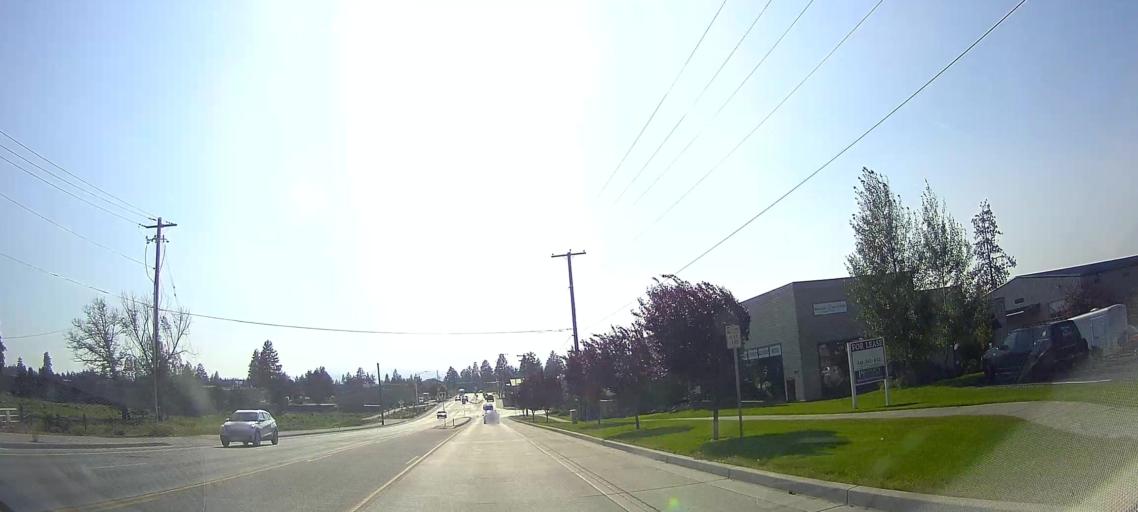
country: US
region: Oregon
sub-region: Deschutes County
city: Bend
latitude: 44.0371
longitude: -121.2863
